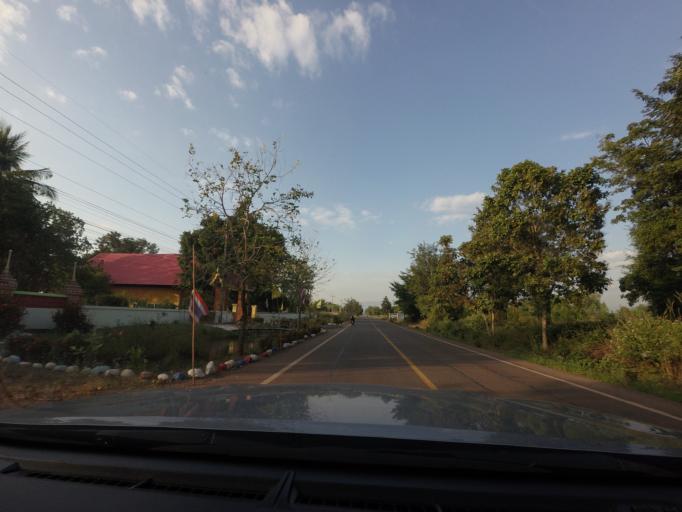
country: TH
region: Phitsanulok
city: Noen Maprang
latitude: 16.6199
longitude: 100.6190
